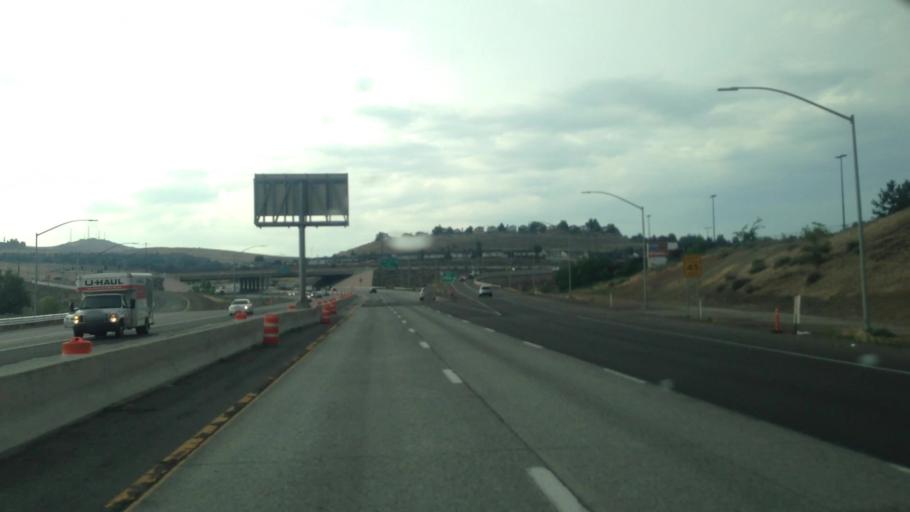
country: US
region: Nevada
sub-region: Washoe County
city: Reno
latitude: 39.5522
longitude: -119.7879
